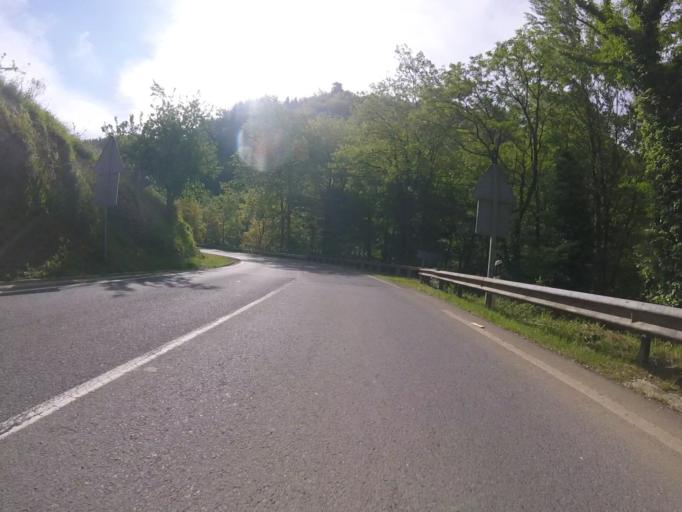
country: ES
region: Basque Country
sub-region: Provincia de Guipuzcoa
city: Azkoitia
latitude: 43.1557
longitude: -2.3389
